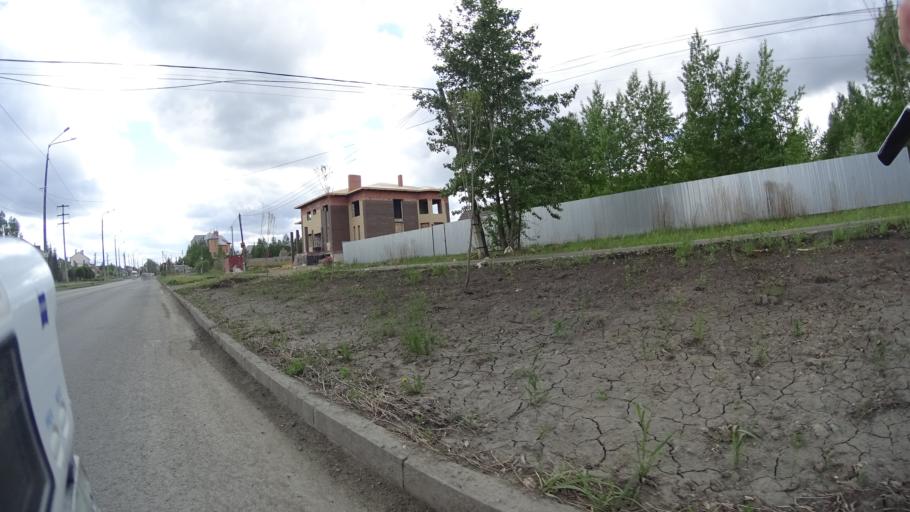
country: RU
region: Chelyabinsk
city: Sargazy
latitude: 55.1544
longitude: 61.2783
